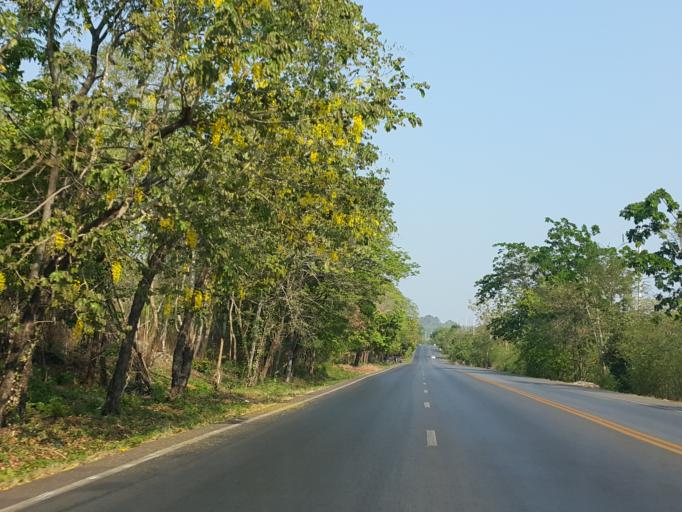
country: TH
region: Kanchanaburi
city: Sai Yok
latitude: 14.1077
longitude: 99.2160
